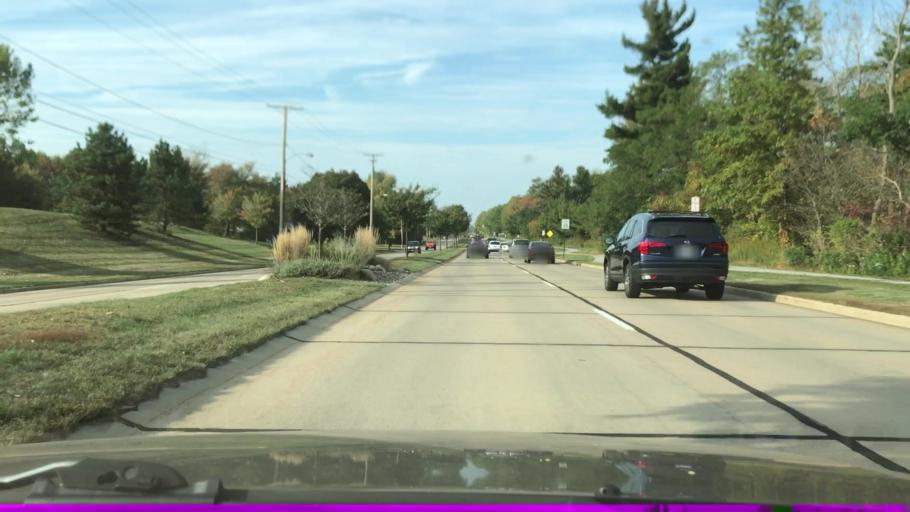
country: US
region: Ohio
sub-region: Cuyahoga County
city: Mayfield
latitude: 41.5658
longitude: -81.4393
